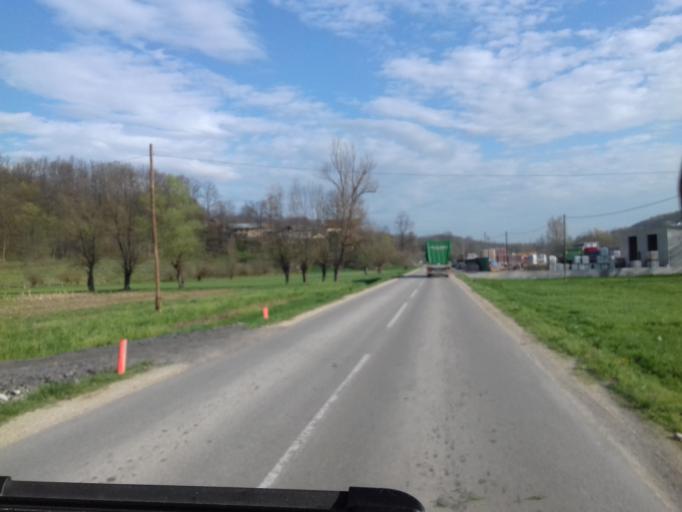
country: BA
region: Federation of Bosnia and Herzegovina
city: Tesanjka
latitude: 44.6521
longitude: 18.0167
